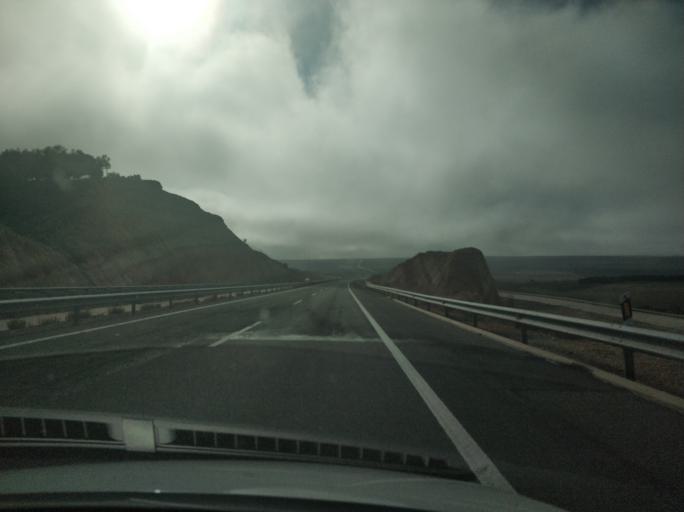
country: ES
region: Castille and Leon
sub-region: Provincia de Soria
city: Adradas
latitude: 41.2927
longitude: -2.4766
